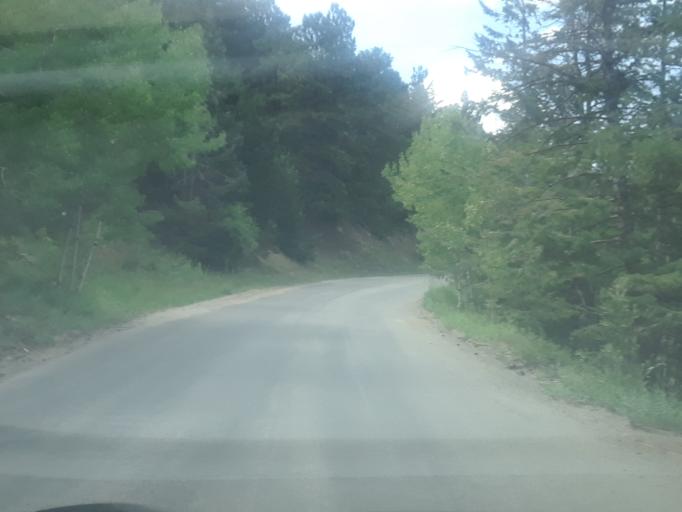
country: US
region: Colorado
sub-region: Boulder County
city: Boulder
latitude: 40.0699
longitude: -105.3846
